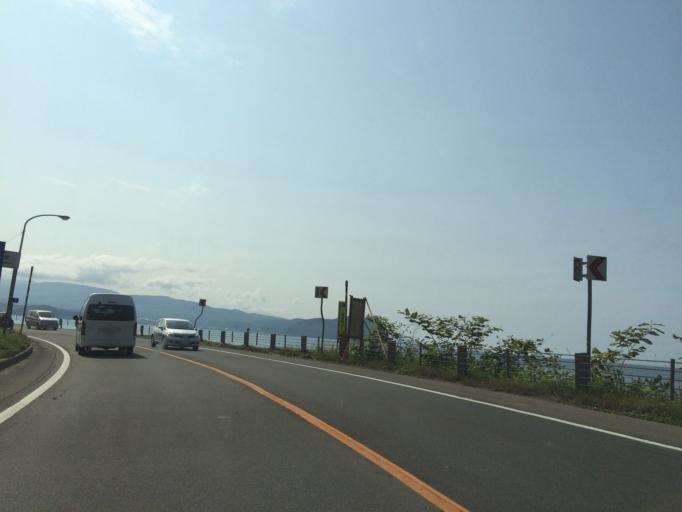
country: JP
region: Hokkaido
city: Yoichi
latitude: 43.1981
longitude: 140.8458
